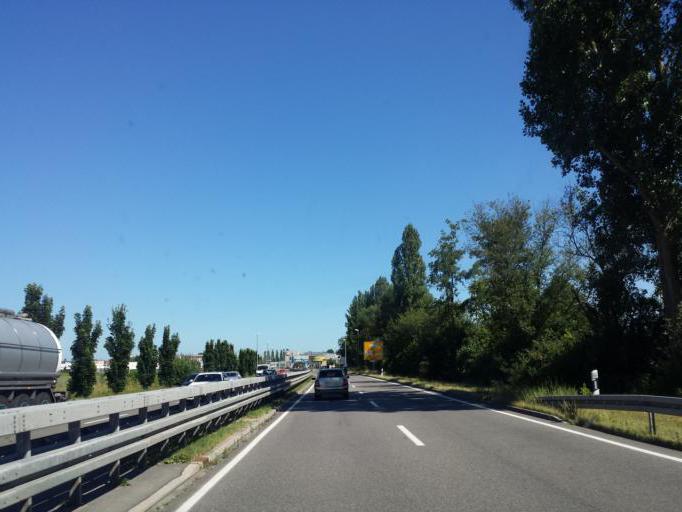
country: CH
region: Thurgau
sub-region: Kreuzlingen District
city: Gottlieben
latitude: 47.6796
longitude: 9.1409
